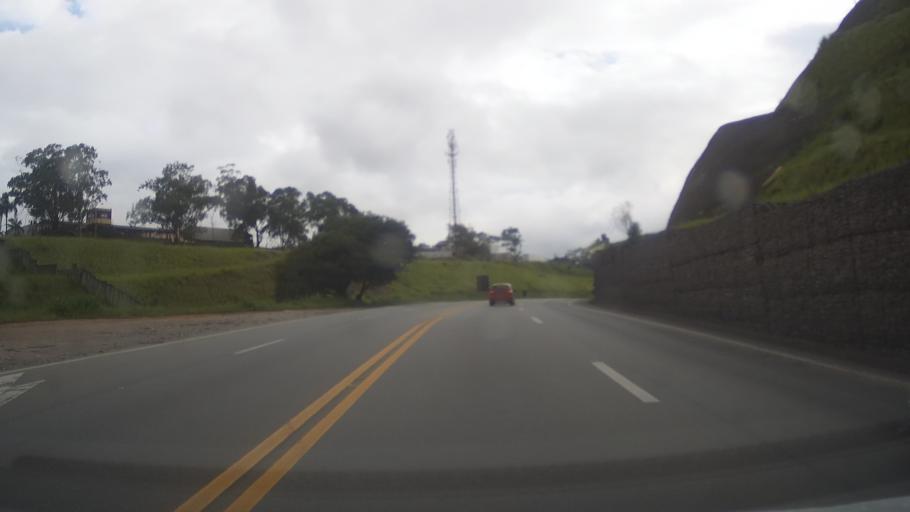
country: BR
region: Sao Paulo
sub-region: Cajamar
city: Cajamar
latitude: -23.3361
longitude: -46.8238
